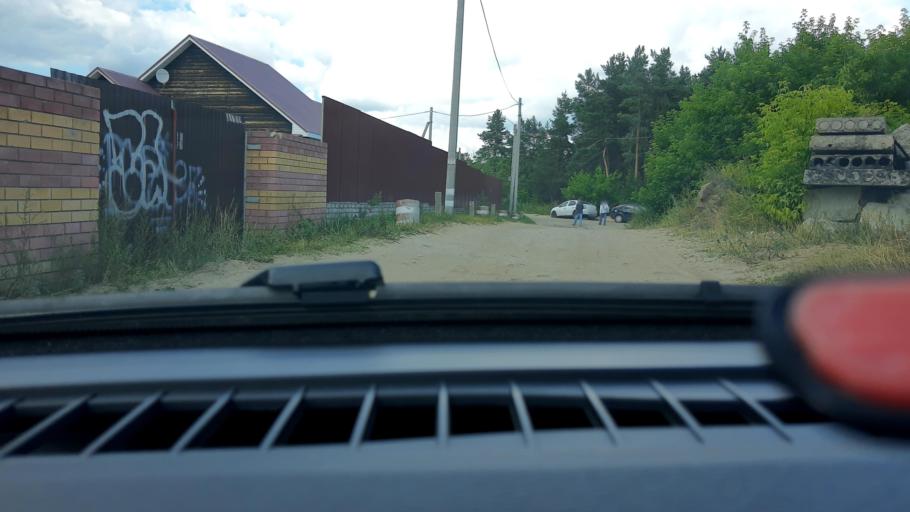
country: RU
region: Nizjnij Novgorod
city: Gorbatovka
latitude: 56.3809
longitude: 43.7651
